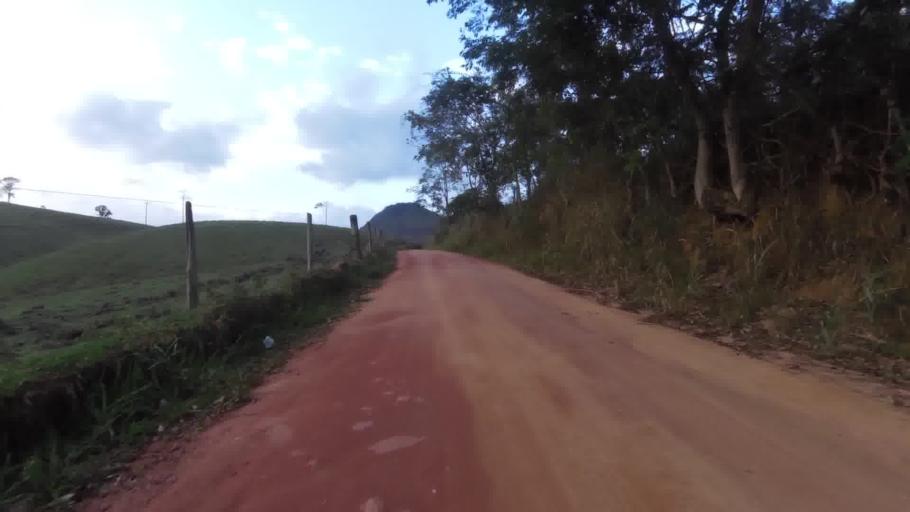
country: BR
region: Espirito Santo
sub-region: Guarapari
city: Guarapari
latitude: -20.6690
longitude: -40.6105
